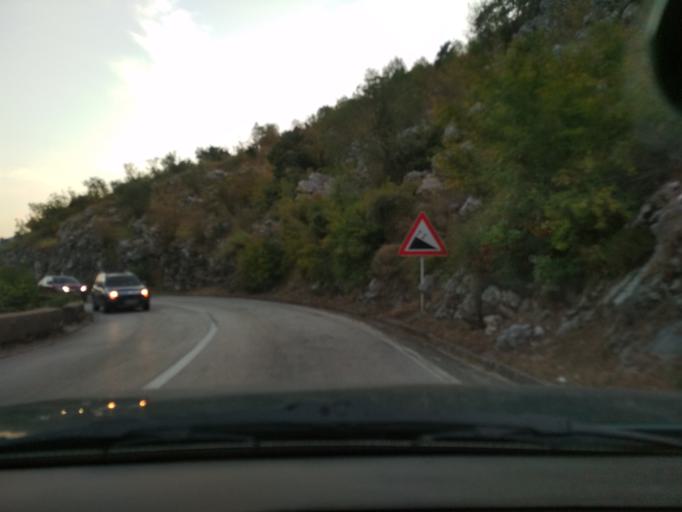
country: ME
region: Kotor
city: Risan
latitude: 42.5133
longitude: 18.6814
